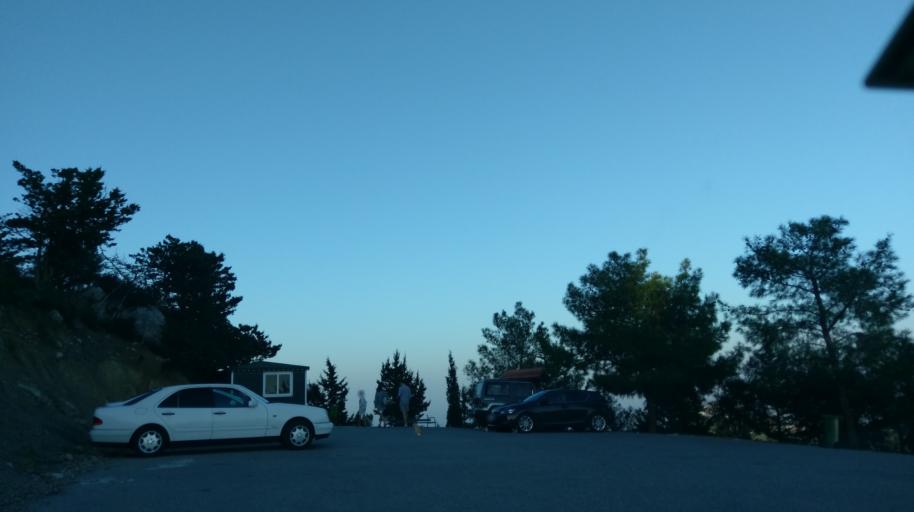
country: CY
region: Ammochostos
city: Trikomo
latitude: 35.4061
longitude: 33.9237
